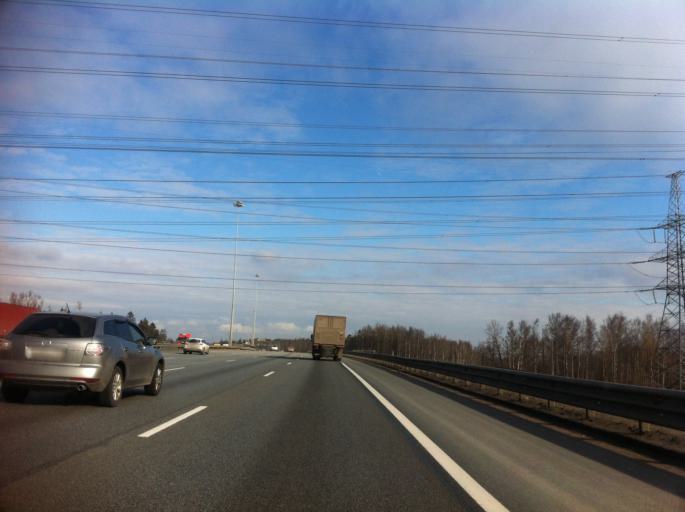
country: RU
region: St.-Petersburg
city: Krasnogvargeisky
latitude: 59.9293
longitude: 30.5354
